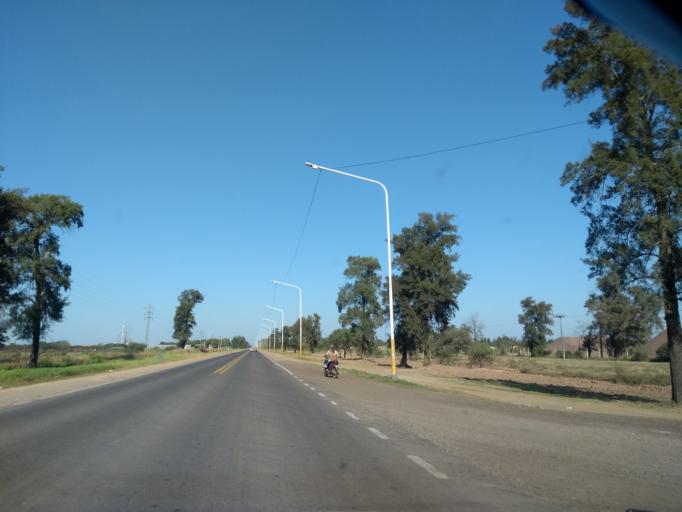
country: AR
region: Chaco
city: Presidencia Roque Saenz Pena
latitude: -26.7824
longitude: -60.4052
